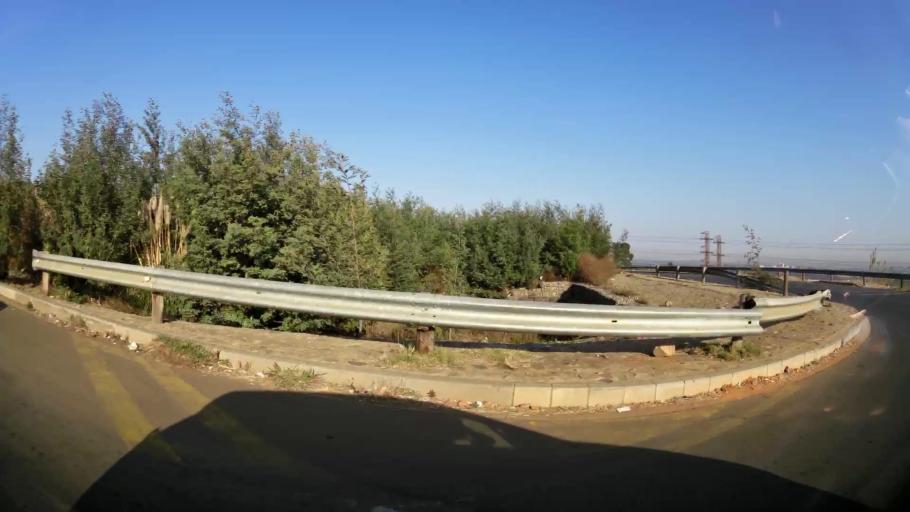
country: ZA
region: Gauteng
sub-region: City of Johannesburg Metropolitan Municipality
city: Modderfontein
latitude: -26.1533
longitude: 28.1876
